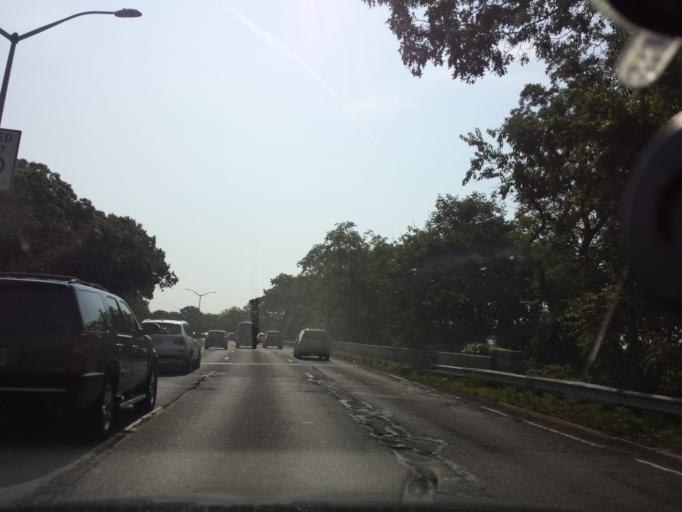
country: US
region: New York
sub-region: Kings County
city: Coney Island
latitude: 40.5846
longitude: -73.9514
